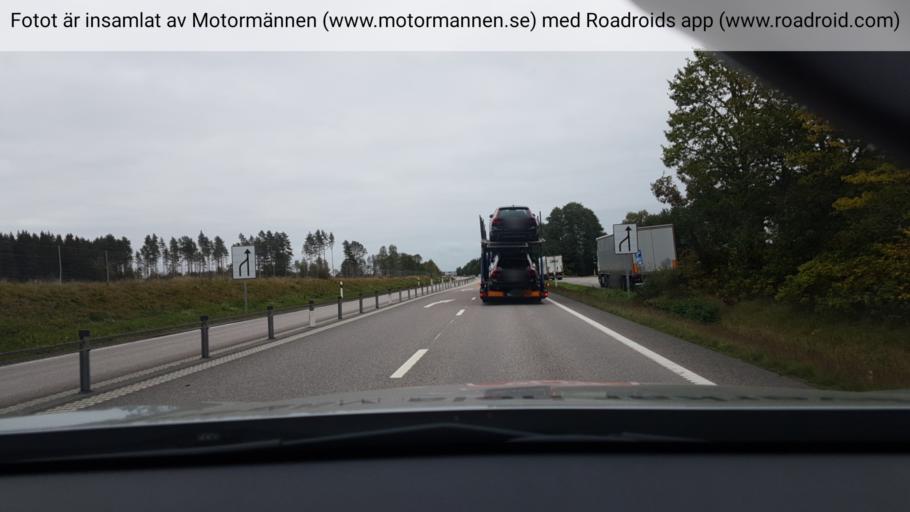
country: SE
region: Vaestra Goetaland
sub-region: Lidkopings Kommun
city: Vinninga
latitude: 58.3516
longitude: 13.3097
